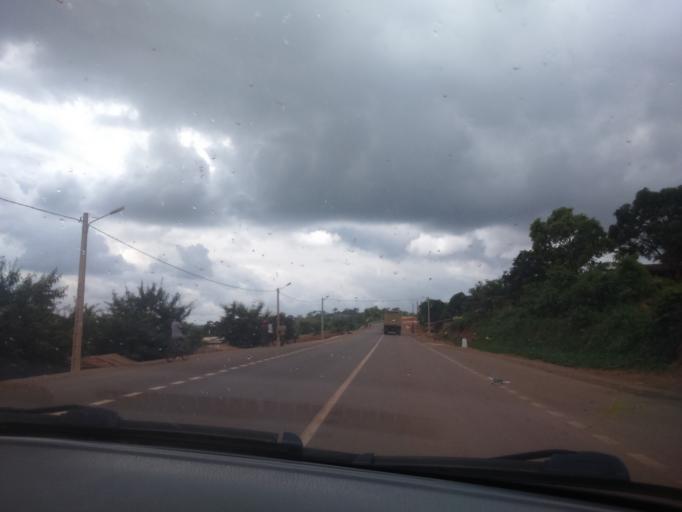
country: CI
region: Moyen-Comoe
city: Abengourou
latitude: 6.6409
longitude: -3.7148
